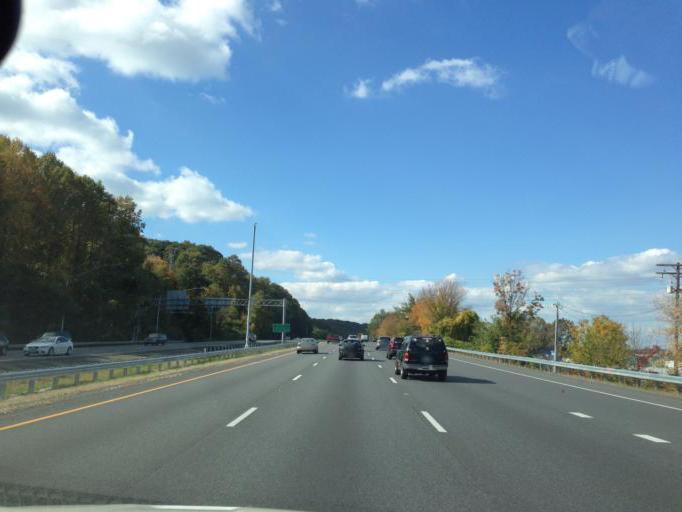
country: US
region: Maryland
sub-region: Baltimore County
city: Mays Chapel
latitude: 39.4565
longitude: -76.6494
